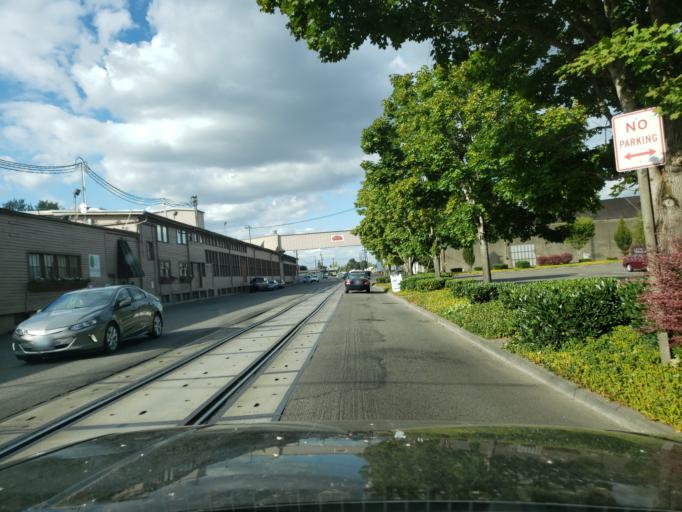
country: US
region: Oregon
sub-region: Marion County
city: Salem
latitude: 44.9516
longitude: -123.0367
